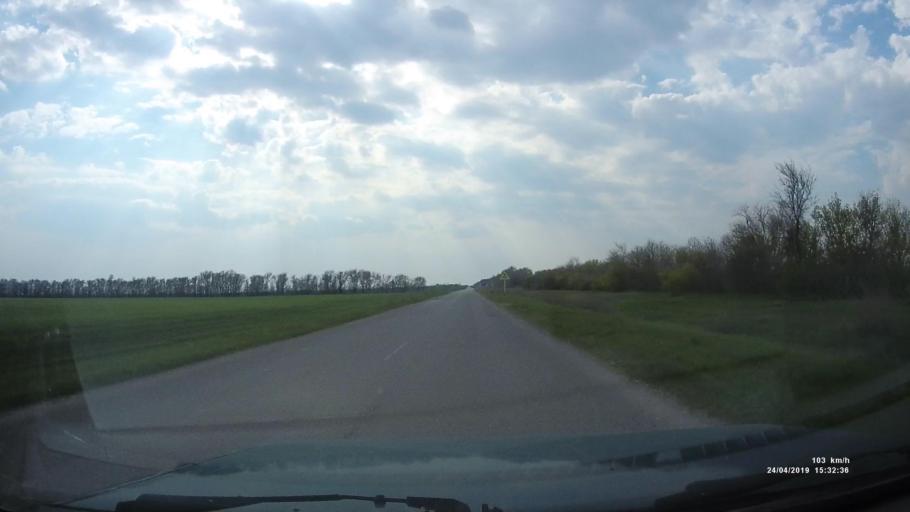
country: RU
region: Rostov
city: Remontnoye
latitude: 46.5996
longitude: 42.9564
